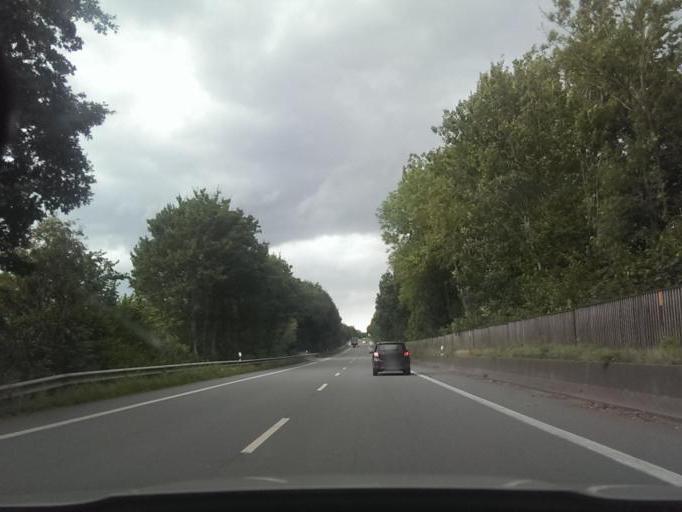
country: DE
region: North Rhine-Westphalia
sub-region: Regierungsbezirk Detmold
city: Steinheim
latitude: 51.8756
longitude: 9.1016
